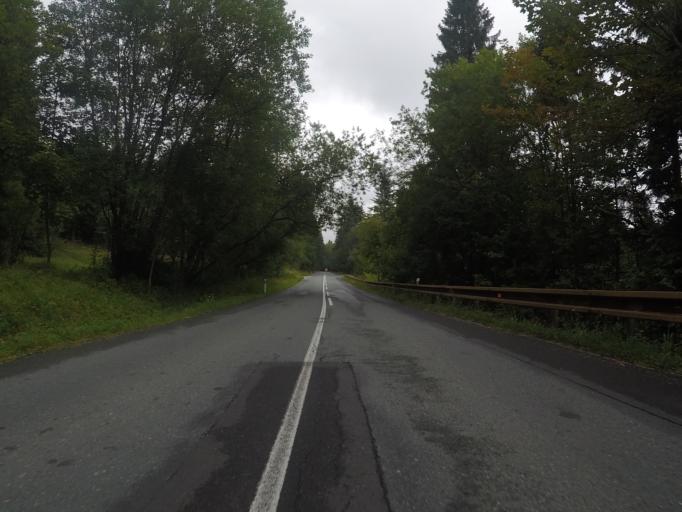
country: SK
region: Kosicky
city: Spisska Nova Ves
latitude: 48.8815
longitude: 20.5366
